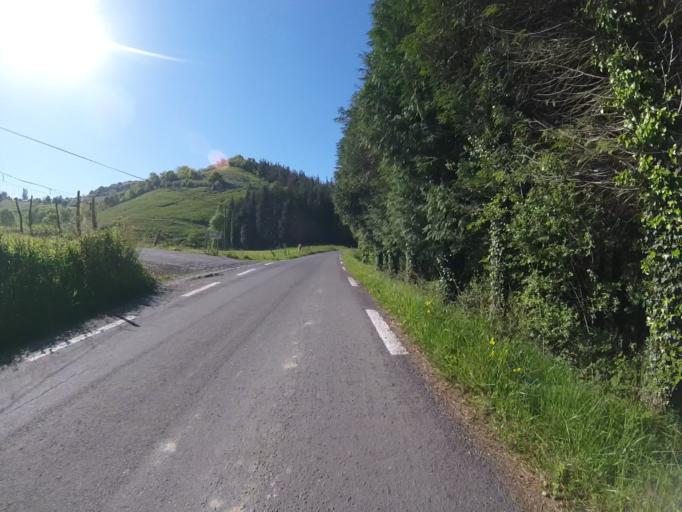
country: ES
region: Basque Country
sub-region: Provincia de Guipuzcoa
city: Aizarnazabal
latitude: 43.2273
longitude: -2.2142
